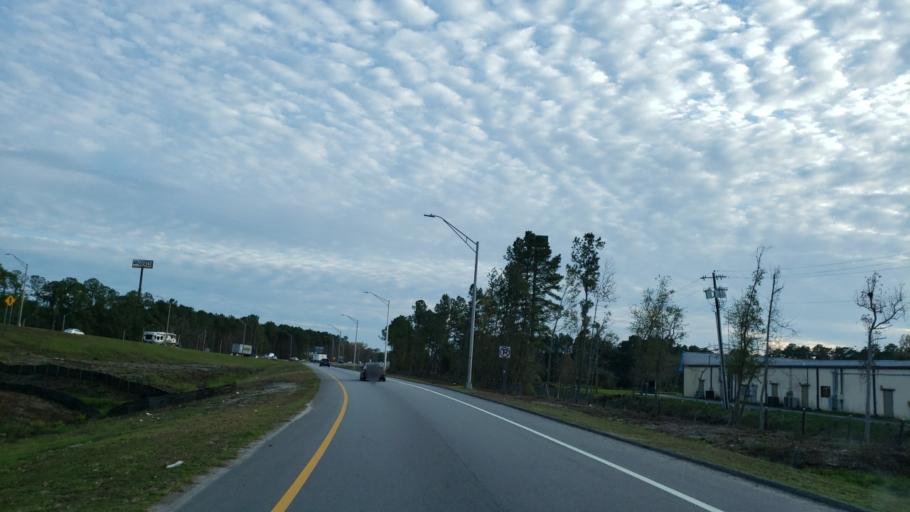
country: US
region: Georgia
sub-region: Chatham County
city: Pooler
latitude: 32.1115
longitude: -81.2389
